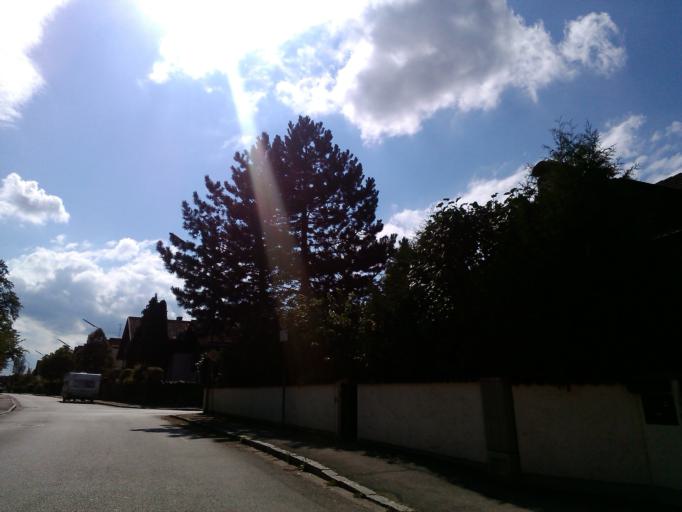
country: DE
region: Bavaria
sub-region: Upper Bavaria
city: Gauting
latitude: 48.0696
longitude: 11.3829
